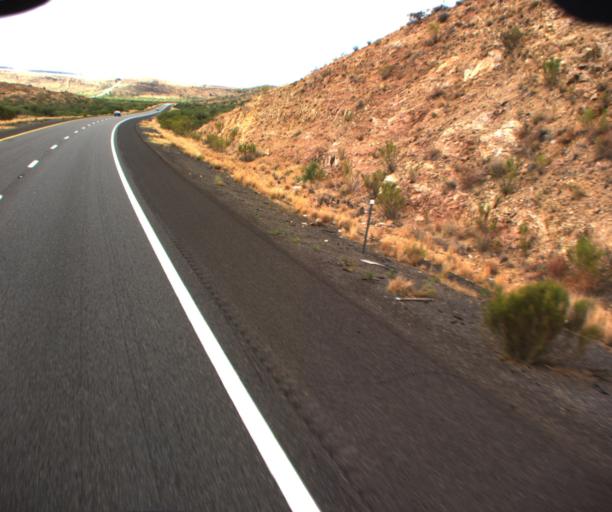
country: US
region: Arizona
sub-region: Yavapai County
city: Cordes Lakes
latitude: 34.2528
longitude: -112.1140
